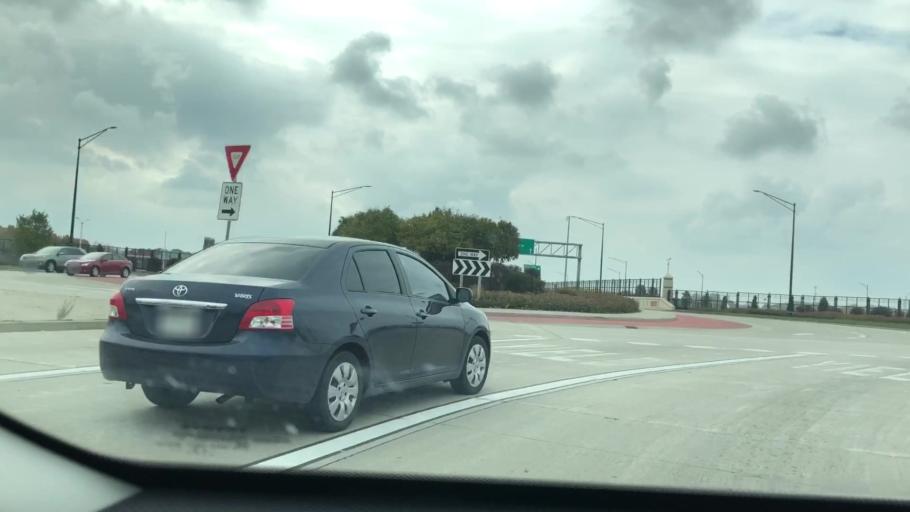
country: US
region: Wisconsin
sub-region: Brown County
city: Howard
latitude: 44.5242
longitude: -88.0804
